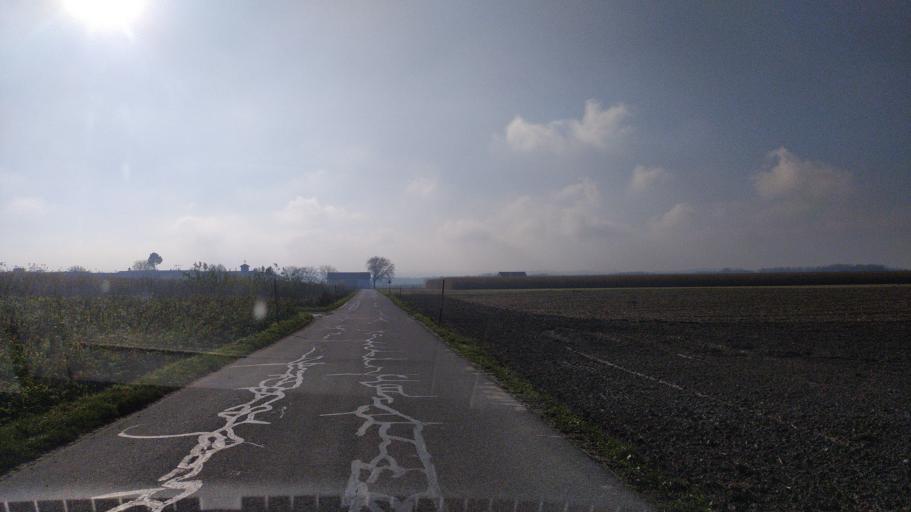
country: AT
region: Upper Austria
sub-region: Politischer Bezirk Perg
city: Perg
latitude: 48.1991
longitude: 14.6517
